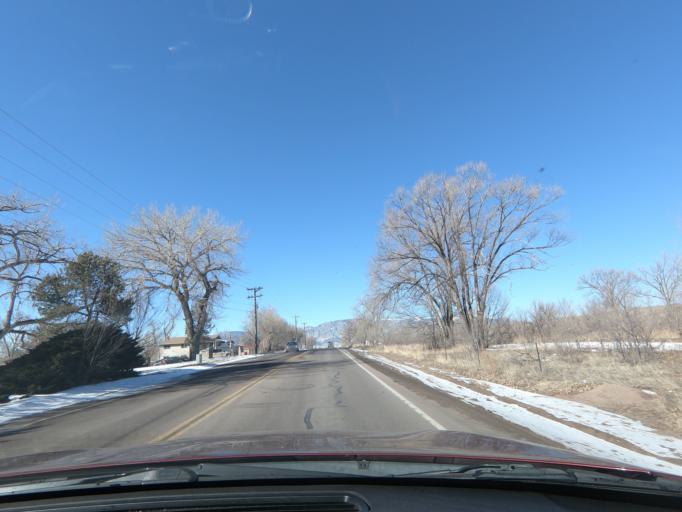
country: US
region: Colorado
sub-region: El Paso County
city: Security-Widefield
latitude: 38.7374
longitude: -104.7146
